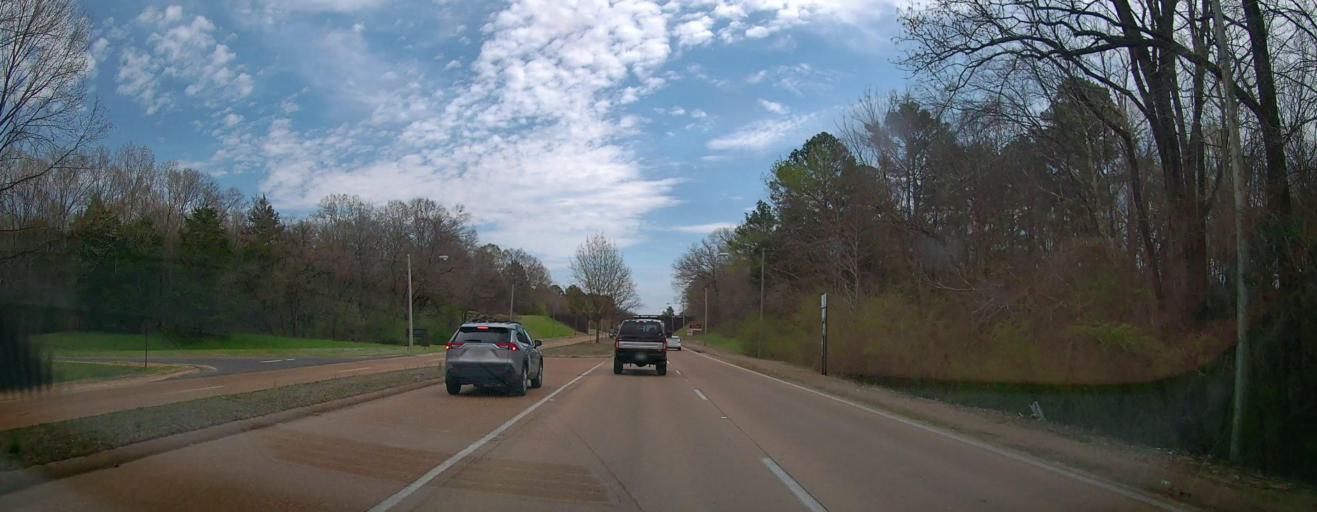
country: US
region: Mississippi
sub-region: Lee County
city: Tupelo
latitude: 34.2832
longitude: -88.7346
